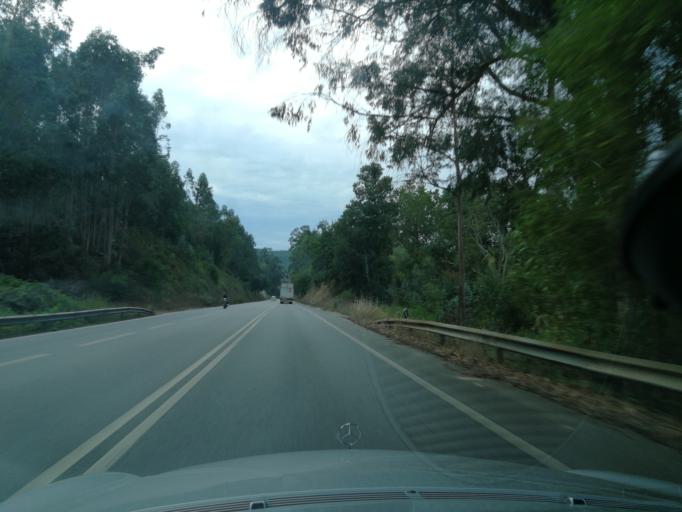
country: PT
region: Aveiro
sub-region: Agueda
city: Valongo
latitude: 40.6289
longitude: -8.4660
